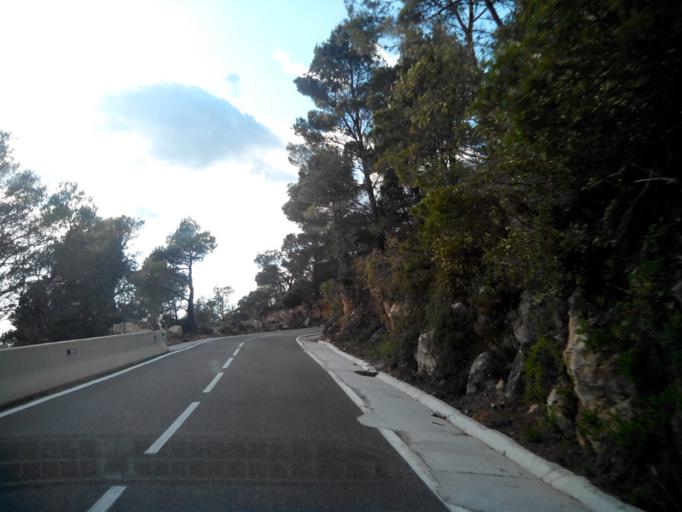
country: ES
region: Catalonia
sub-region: Provincia de Tarragona
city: Vilaplana
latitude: 41.2356
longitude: 1.0590
